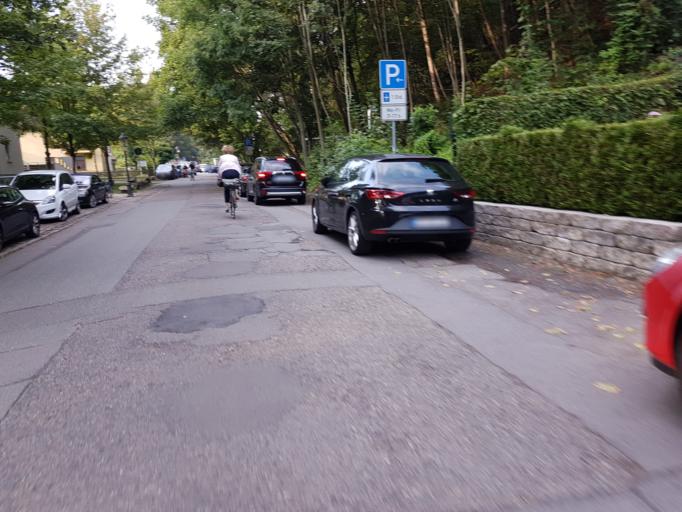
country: DE
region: Saxony
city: Chemnitz
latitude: 50.8467
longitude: 12.9185
